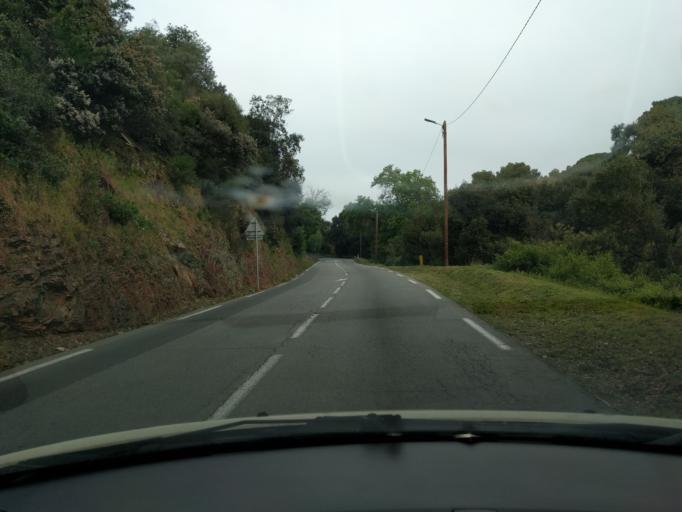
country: FR
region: Provence-Alpes-Cote d'Azur
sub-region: Departement des Alpes-Maritimes
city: La Roquette-sur-Siagne
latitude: 43.5817
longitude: 6.9588
